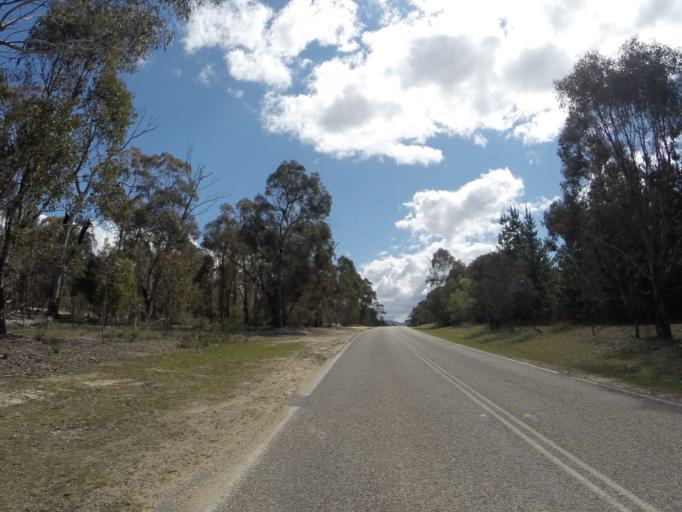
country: AU
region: Australian Capital Territory
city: Macquarie
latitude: -35.3489
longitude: 148.9337
